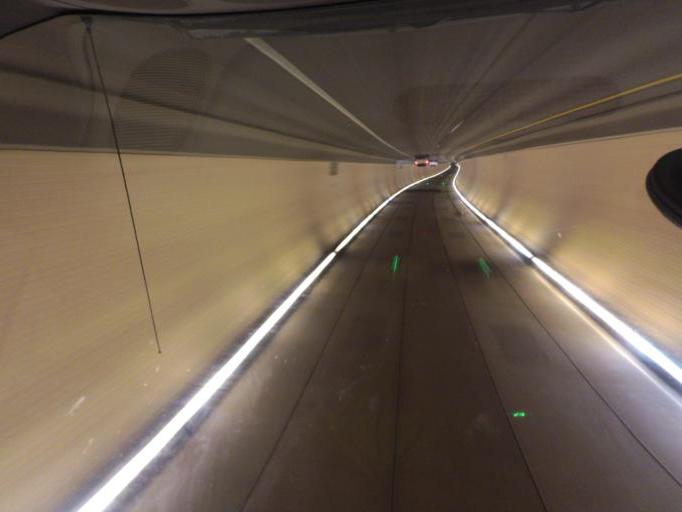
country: US
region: Colorado
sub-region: Garfield County
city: Glenwood Springs
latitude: 39.5864
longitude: -107.1893
